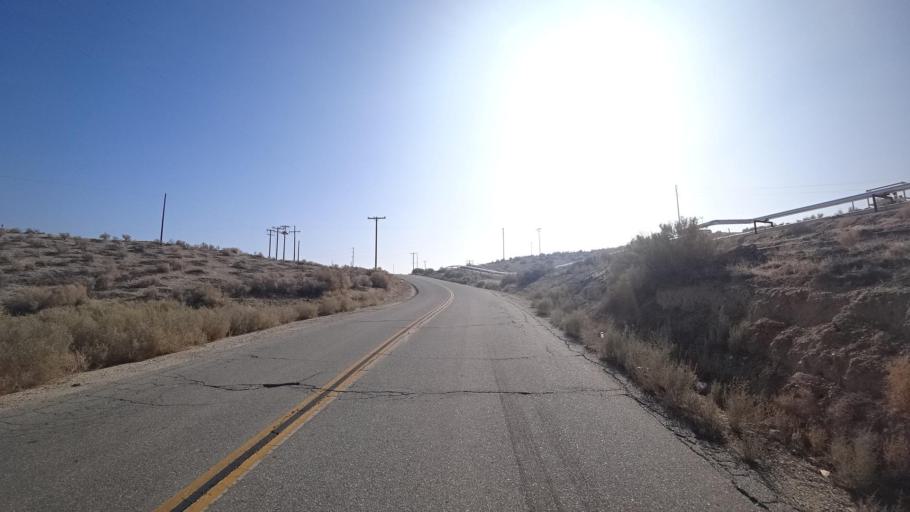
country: US
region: California
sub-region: Kern County
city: Taft Heights
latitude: 35.1454
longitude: -119.5131
